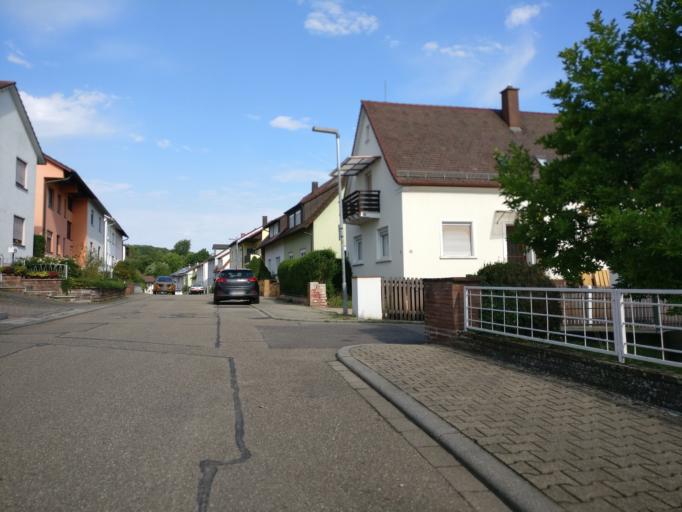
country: DE
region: Baden-Wuerttemberg
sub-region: Karlsruhe Region
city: Woessingen
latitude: 49.0136
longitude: 8.6001
